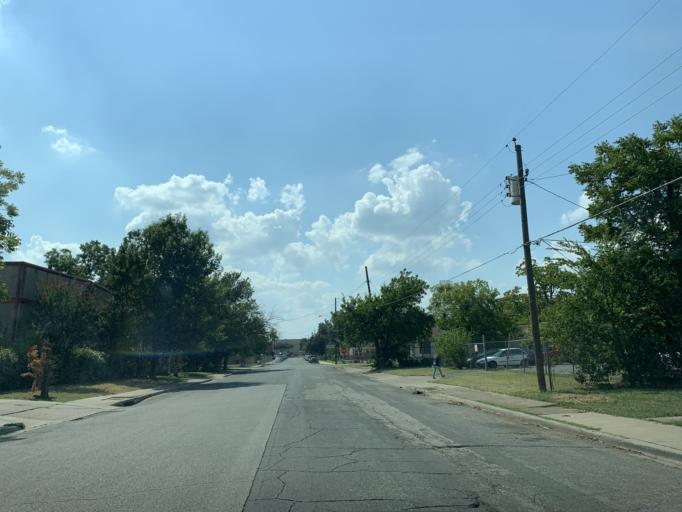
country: US
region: Texas
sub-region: Dallas County
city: Dallas
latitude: 32.7442
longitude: -96.8292
